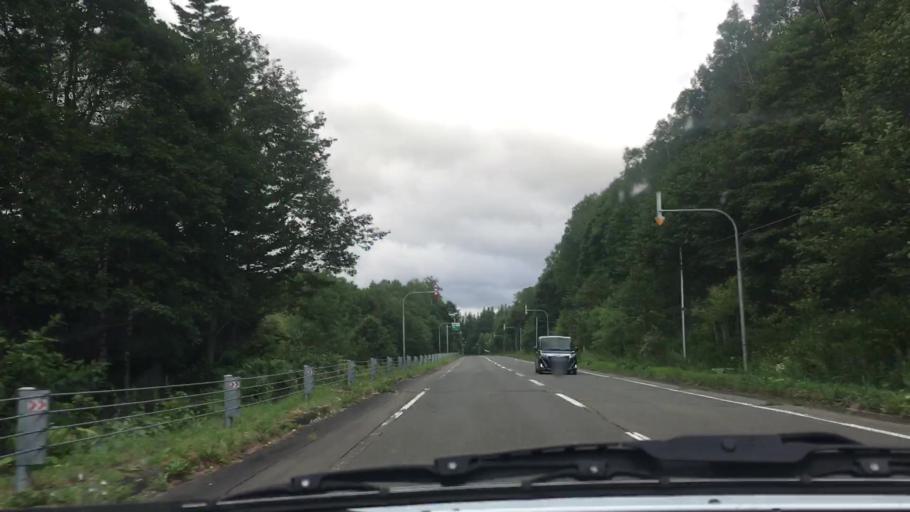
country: JP
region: Hokkaido
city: Shimo-furano
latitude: 43.0588
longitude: 142.6682
